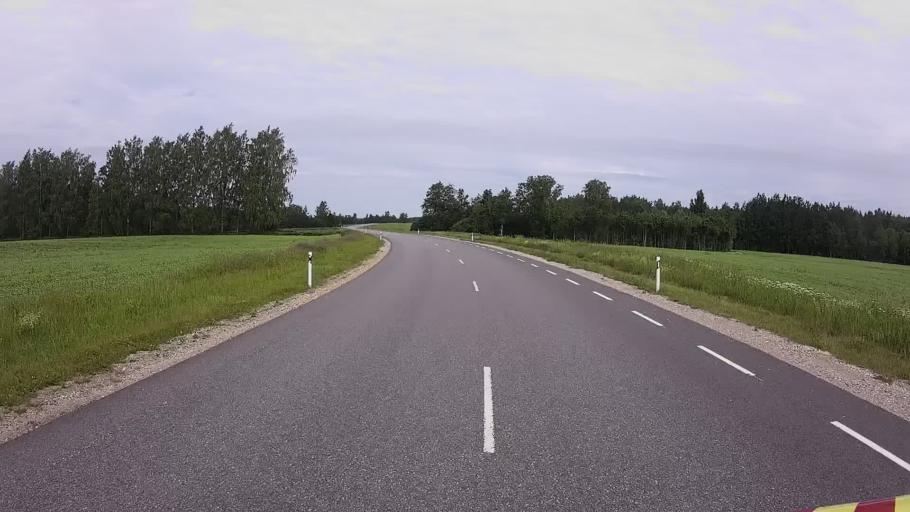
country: EE
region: Viljandimaa
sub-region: Karksi vald
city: Karksi-Nuia
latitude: 58.1583
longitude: 25.5930
